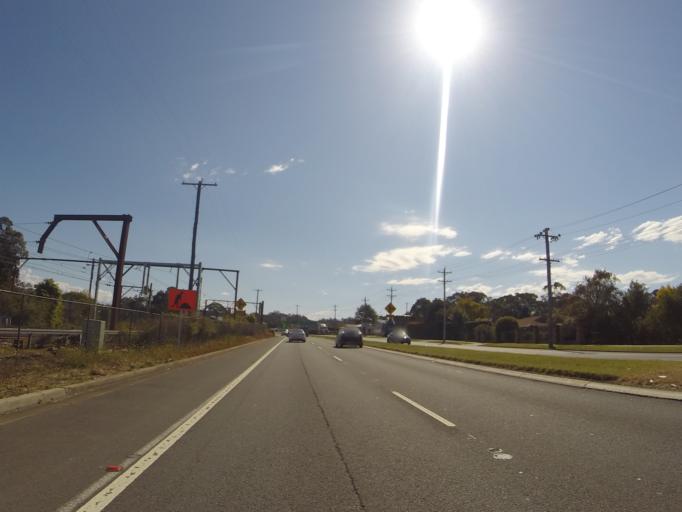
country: AU
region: New South Wales
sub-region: Blue Mountains Municipality
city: Blaxland
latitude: -33.7035
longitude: 150.5834
